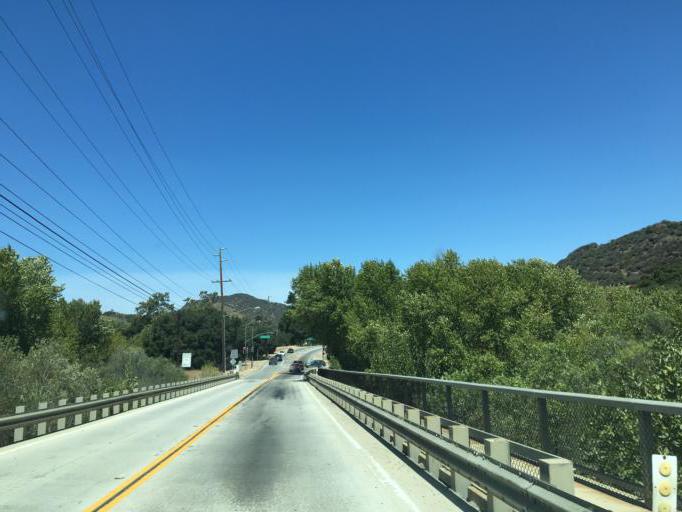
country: US
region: California
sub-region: Los Angeles County
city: Malibu Beach
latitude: 34.0811
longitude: -118.7041
